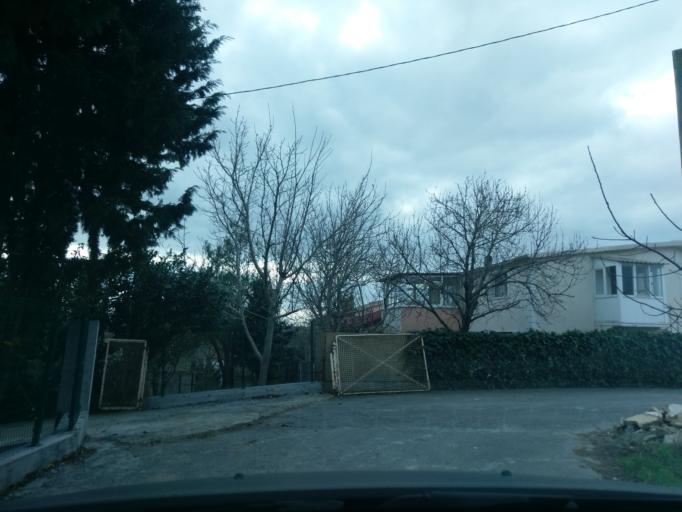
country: TR
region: Istanbul
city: Boyalik
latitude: 41.2723
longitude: 28.6572
